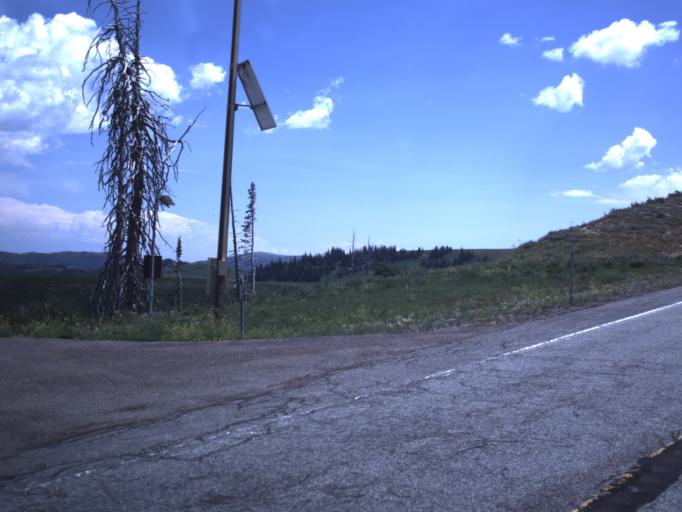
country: US
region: Utah
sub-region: Sanpete County
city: Fairview
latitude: 39.6207
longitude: -111.3137
